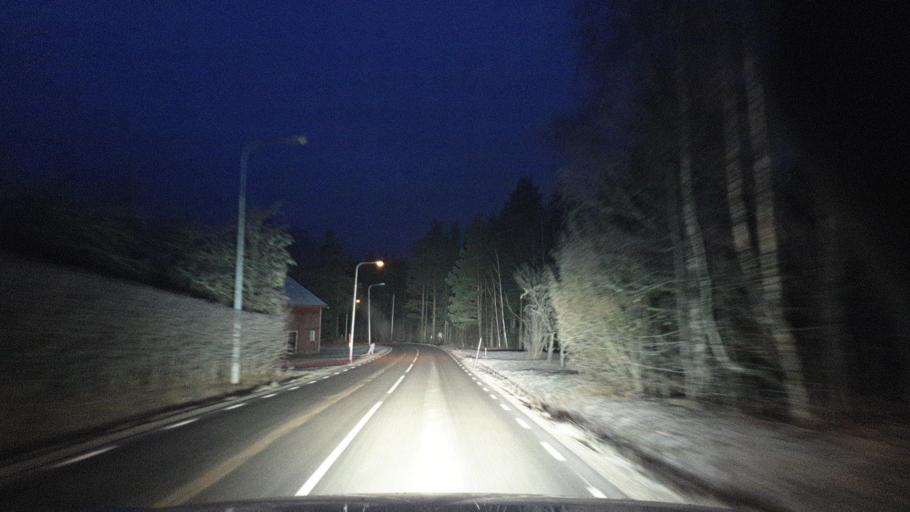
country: SE
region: Vaermland
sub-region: Arvika Kommun
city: Arvika
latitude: 59.5431
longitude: 12.5783
